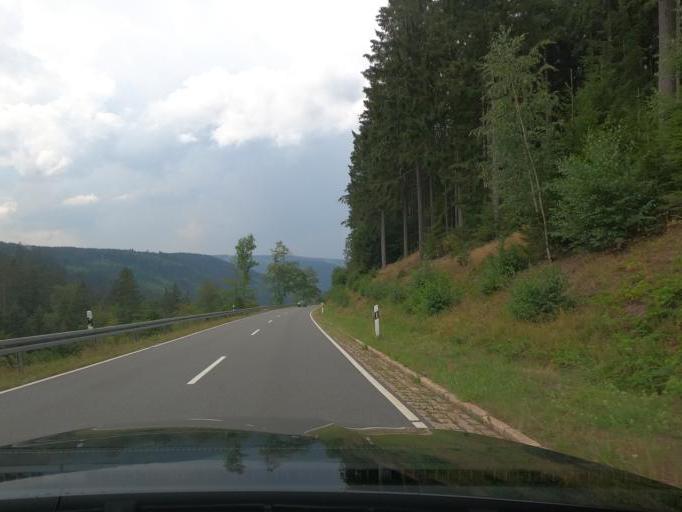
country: DE
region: Lower Saxony
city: Wildemann
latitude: 51.8614
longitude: 10.3162
